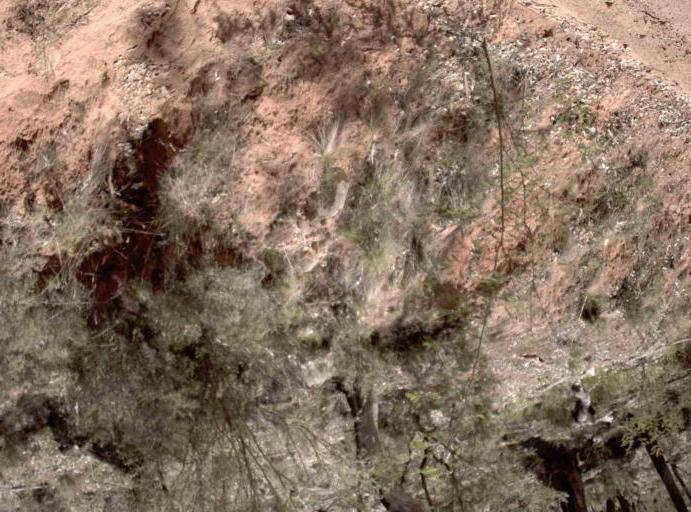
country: AU
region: New South Wales
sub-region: Snowy River
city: Jindabyne
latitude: -37.0594
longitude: 148.5300
